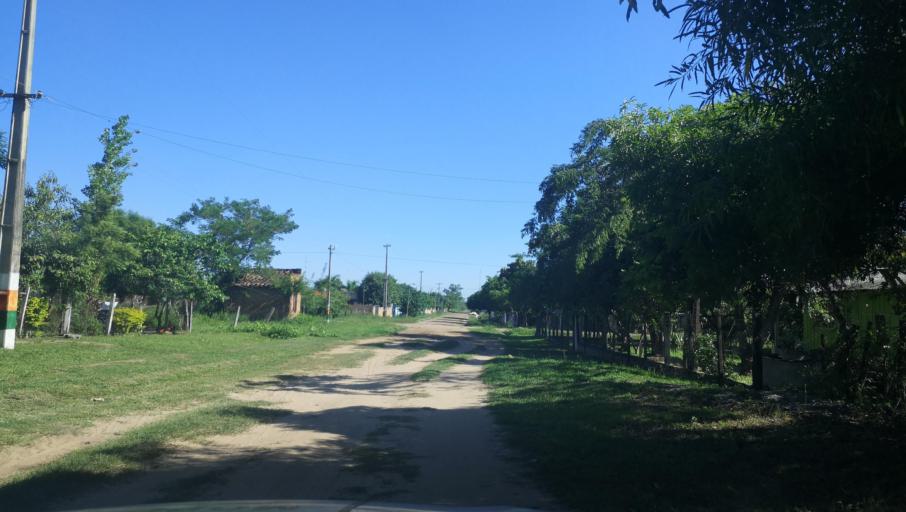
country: PY
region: Caaguazu
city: Carayao
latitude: -25.1948
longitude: -56.3982
